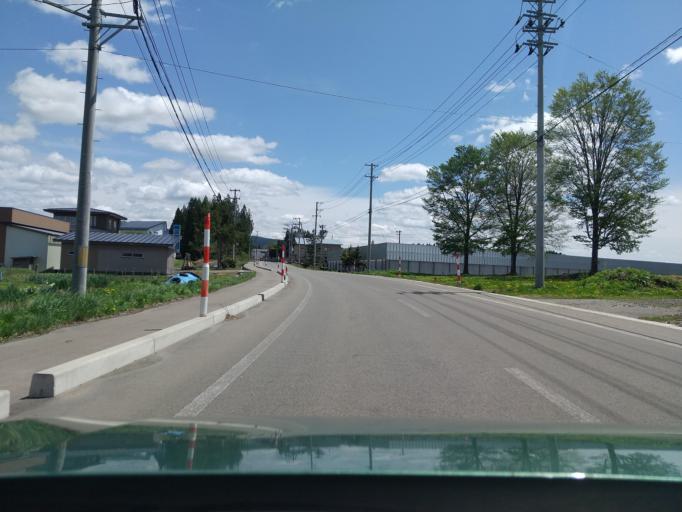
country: JP
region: Akita
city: Yokotemachi
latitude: 39.3513
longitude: 140.5498
